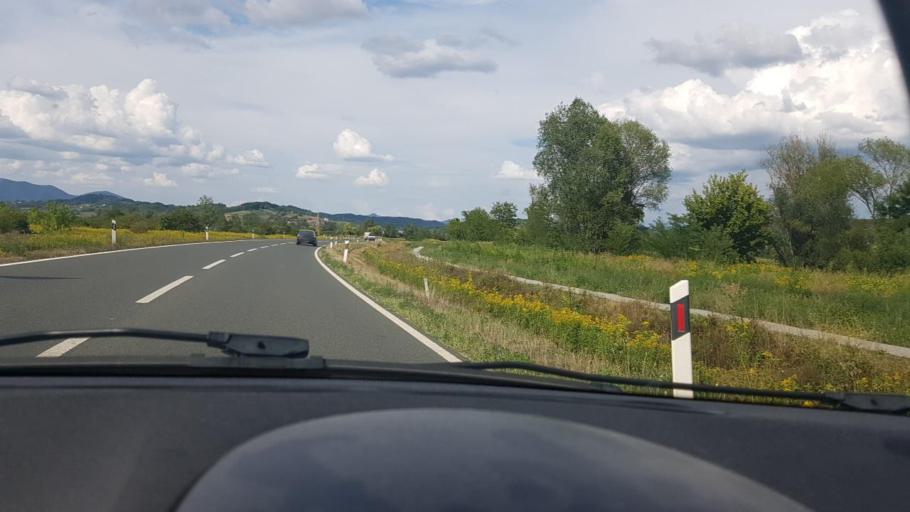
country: HR
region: Krapinsko-Zagorska
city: Zabok
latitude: 46.0575
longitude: 15.9142
